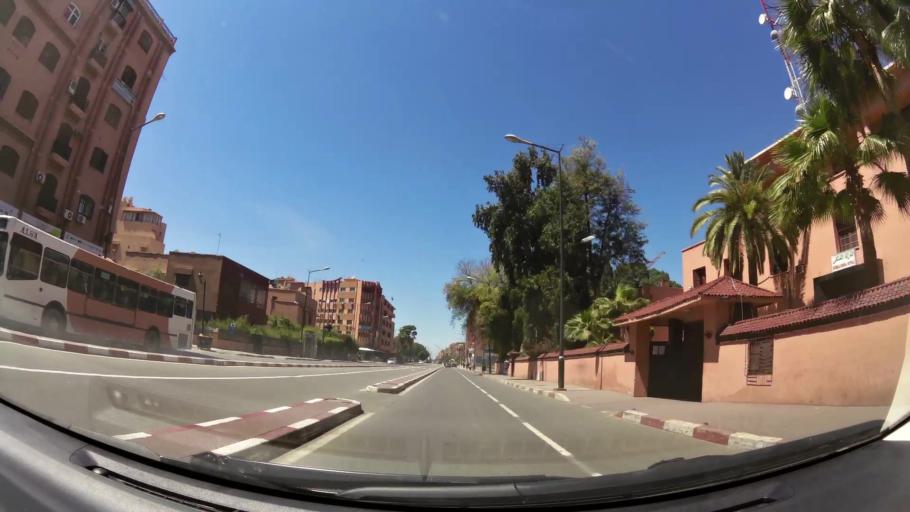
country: MA
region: Marrakech-Tensift-Al Haouz
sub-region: Marrakech
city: Marrakesh
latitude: 31.6336
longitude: -8.0051
